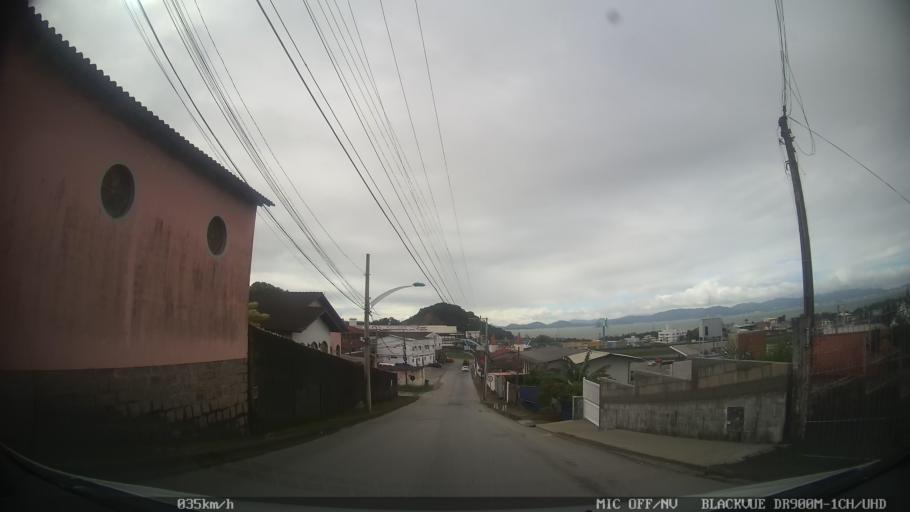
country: BR
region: Santa Catarina
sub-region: Biguacu
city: Biguacu
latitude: -27.5209
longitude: -48.6389
